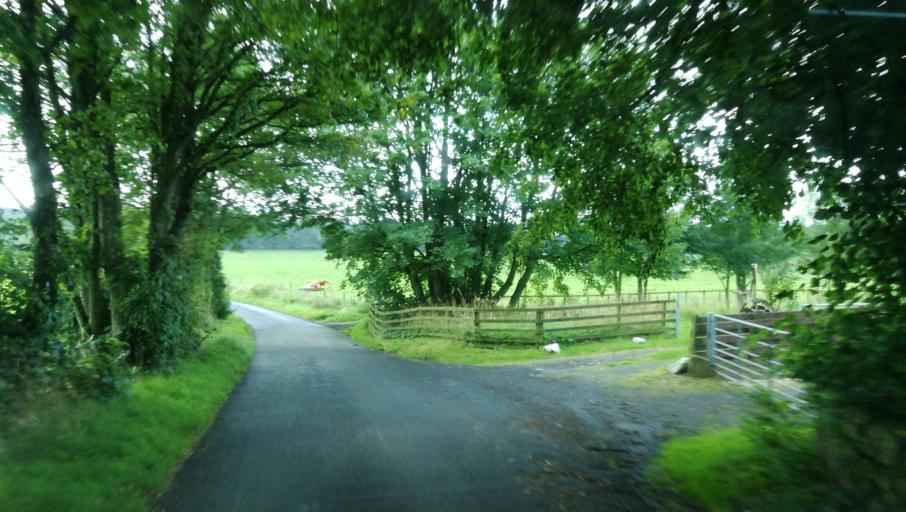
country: GB
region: Scotland
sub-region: Perth and Kinross
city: Alyth
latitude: 56.6250
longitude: -3.2815
